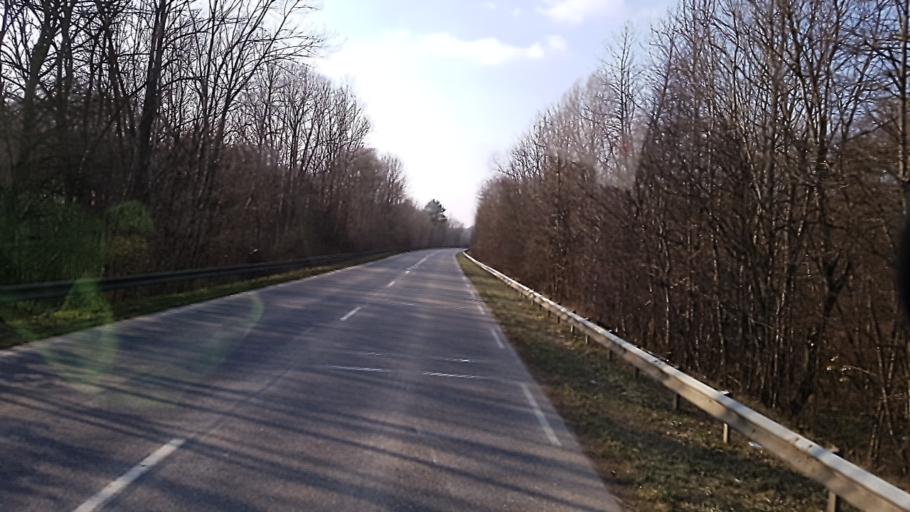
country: FR
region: Alsace
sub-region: Departement du Bas-Rhin
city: Drulingen
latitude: 48.8596
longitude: 7.1910
